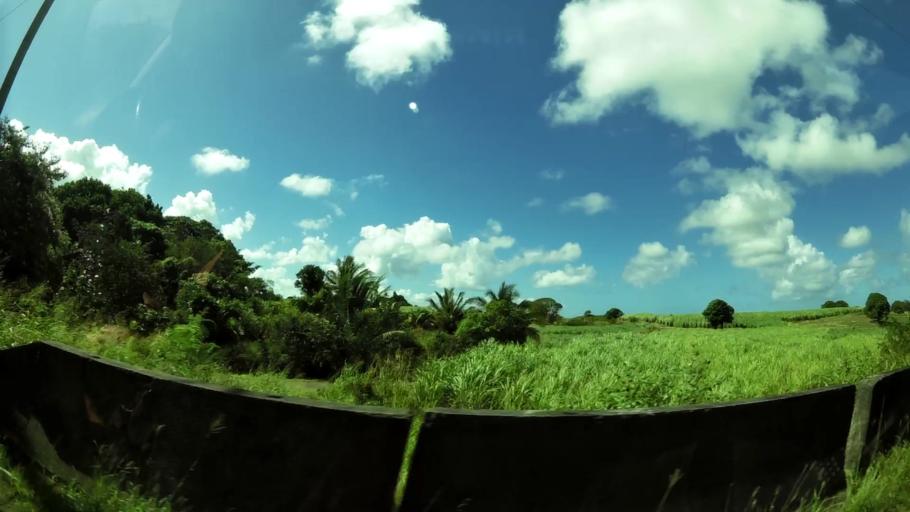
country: GP
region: Guadeloupe
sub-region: Guadeloupe
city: Petit-Canal
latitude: 16.4112
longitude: -61.4693
